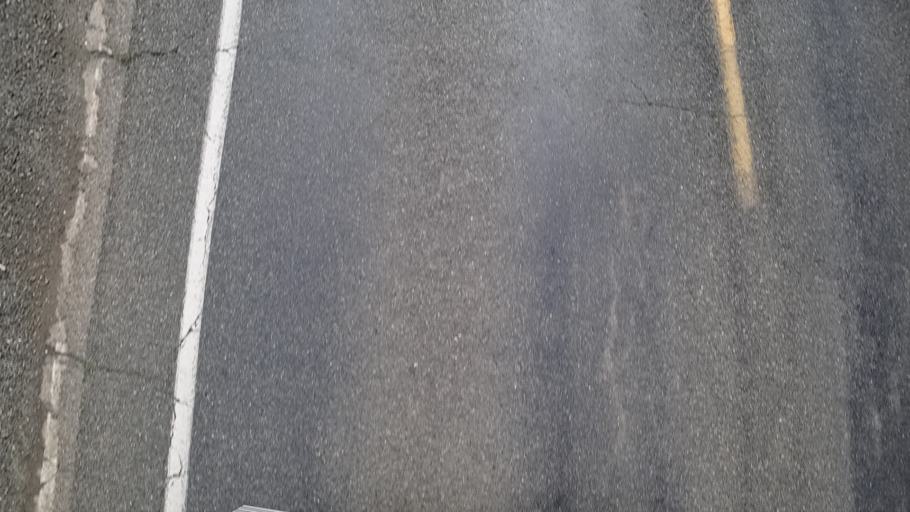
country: US
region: California
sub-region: Butte County
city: Oroville East
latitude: 39.4641
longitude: -121.4528
